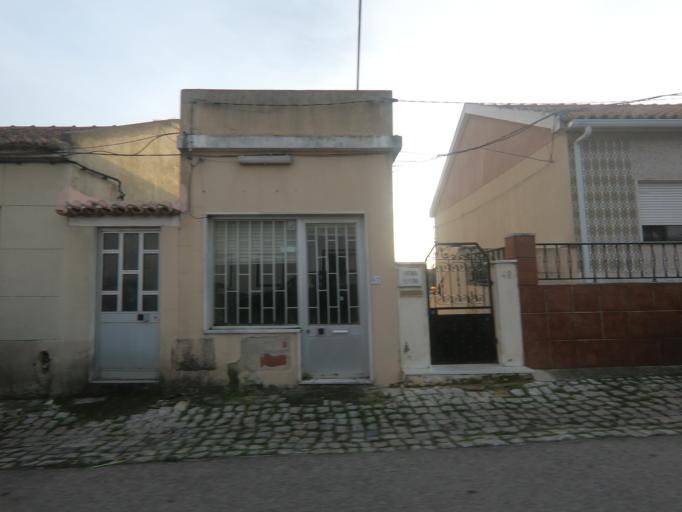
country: PT
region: Setubal
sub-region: Setubal
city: Setubal
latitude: 38.5269
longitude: -8.8651
